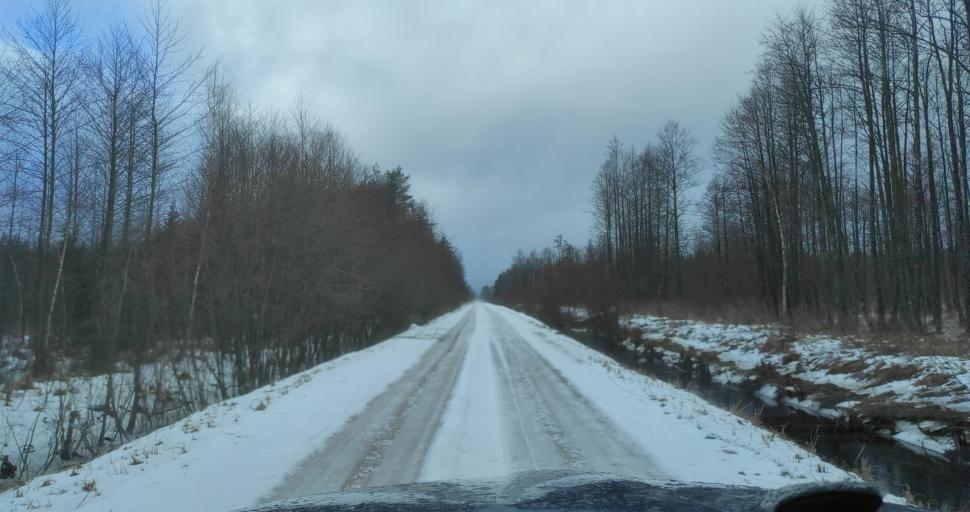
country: LV
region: Dundaga
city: Dundaga
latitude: 57.3960
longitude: 22.1187
